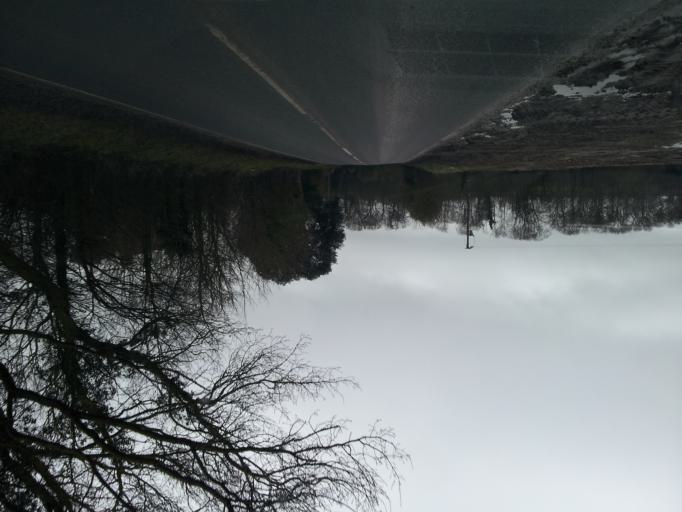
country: GB
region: England
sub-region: Essex
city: Mistley
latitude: 51.9338
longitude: 1.0731
